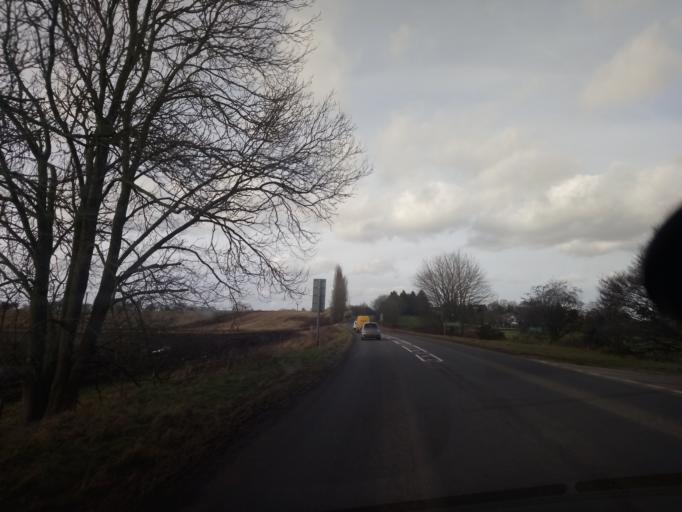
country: GB
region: England
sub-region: Telford and Wrekin
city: Eyton upon the Weald Moors
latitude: 52.7718
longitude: -2.5490
